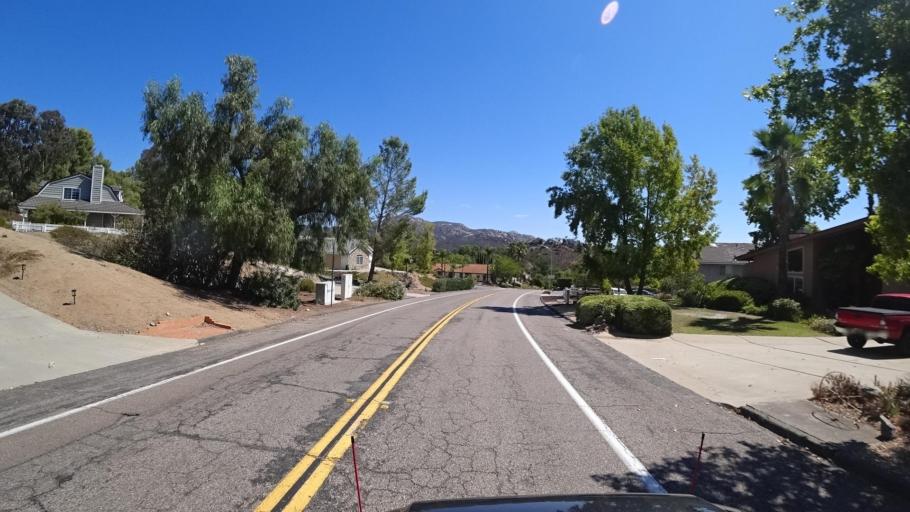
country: US
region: California
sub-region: San Diego County
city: San Diego Country Estates
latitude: 33.0266
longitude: -116.8126
